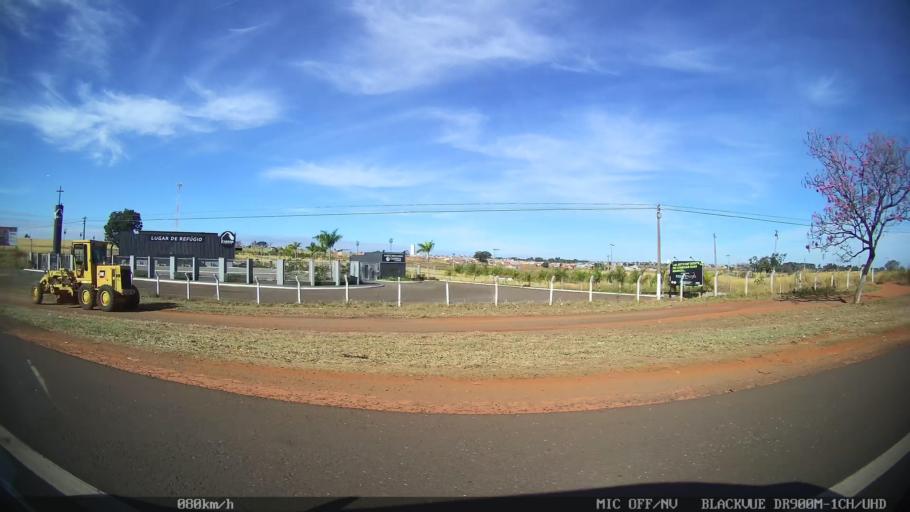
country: BR
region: Sao Paulo
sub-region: Sao Jose Do Rio Preto
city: Sao Jose do Rio Preto
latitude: -20.7450
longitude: -49.3389
